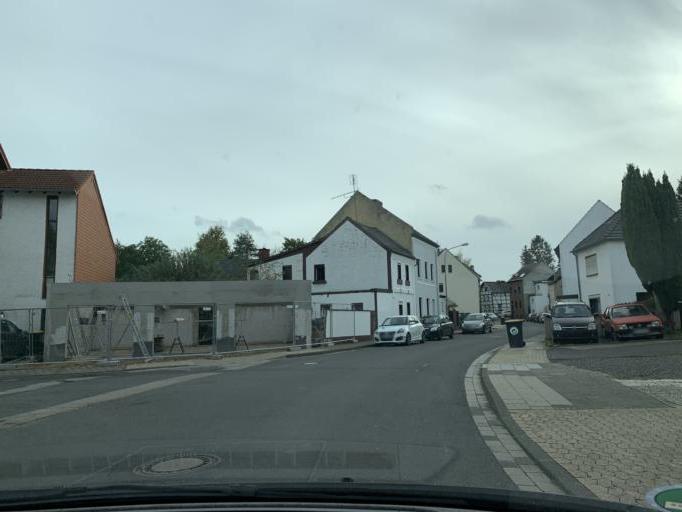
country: DE
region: North Rhine-Westphalia
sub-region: Regierungsbezirk Koln
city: Kreuzau
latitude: 50.7274
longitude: 6.5177
